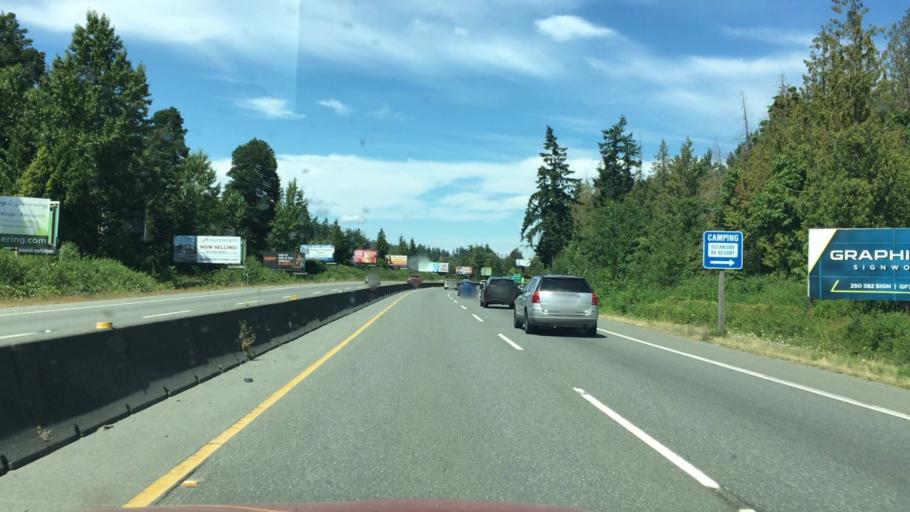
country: CA
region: British Columbia
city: North Saanich
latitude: 48.5838
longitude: -123.4007
